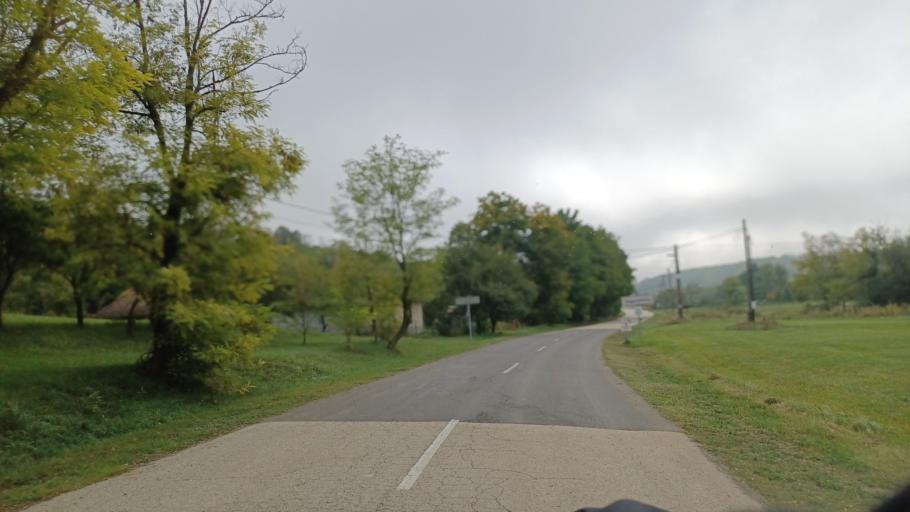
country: HU
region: Tolna
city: Pincehely
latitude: 46.6508
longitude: 18.5173
